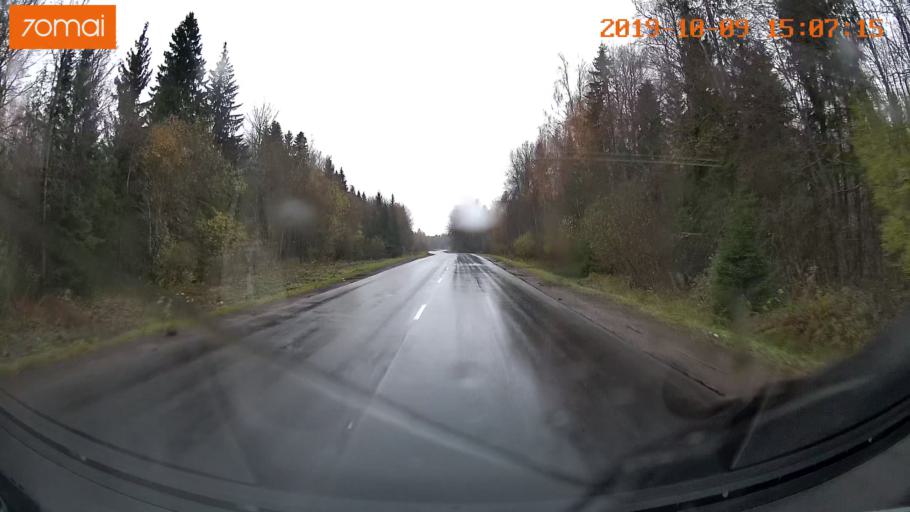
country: RU
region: Kostroma
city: Susanino
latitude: 58.2215
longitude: 41.6520
